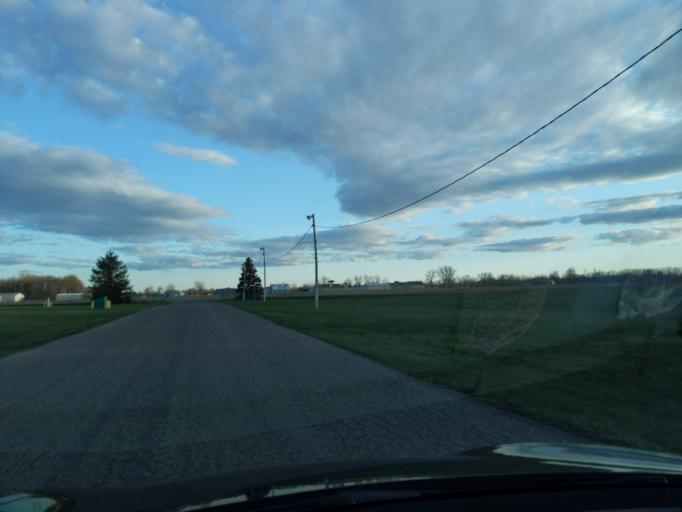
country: US
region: Michigan
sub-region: Ingham County
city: Mason
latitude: 42.5688
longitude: -84.4277
